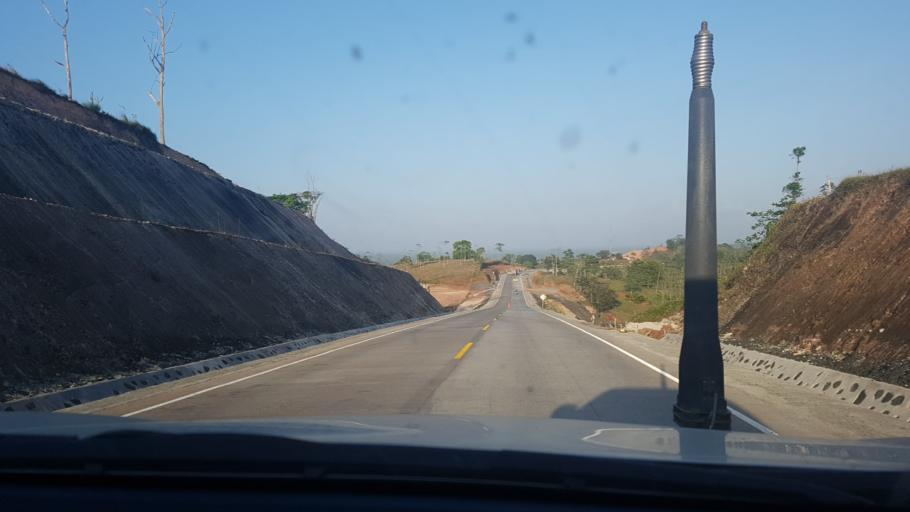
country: NI
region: Atlantico Sur
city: Rama
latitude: 11.8348
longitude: -84.0756
